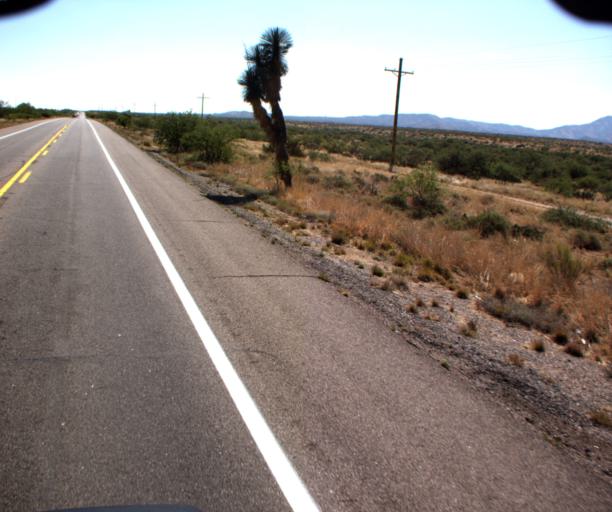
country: US
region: Arizona
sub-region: Pima County
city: Catalina
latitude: 32.5951
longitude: -110.8849
